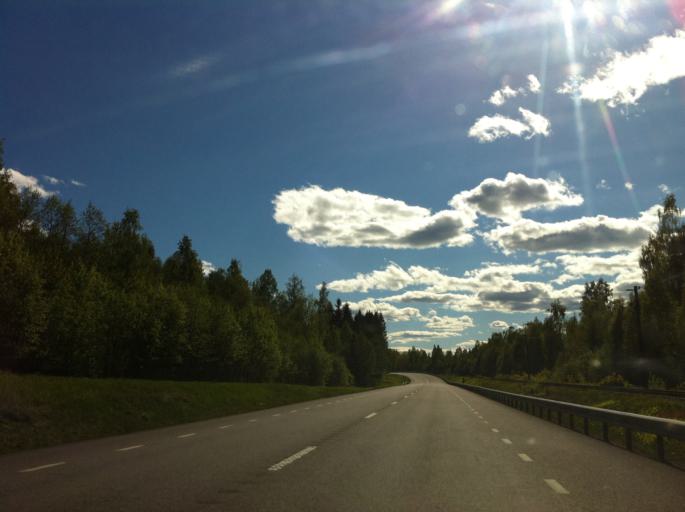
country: SE
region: Dalarna
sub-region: Rattviks Kommun
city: Raettvik
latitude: 60.8364
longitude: 15.0899
